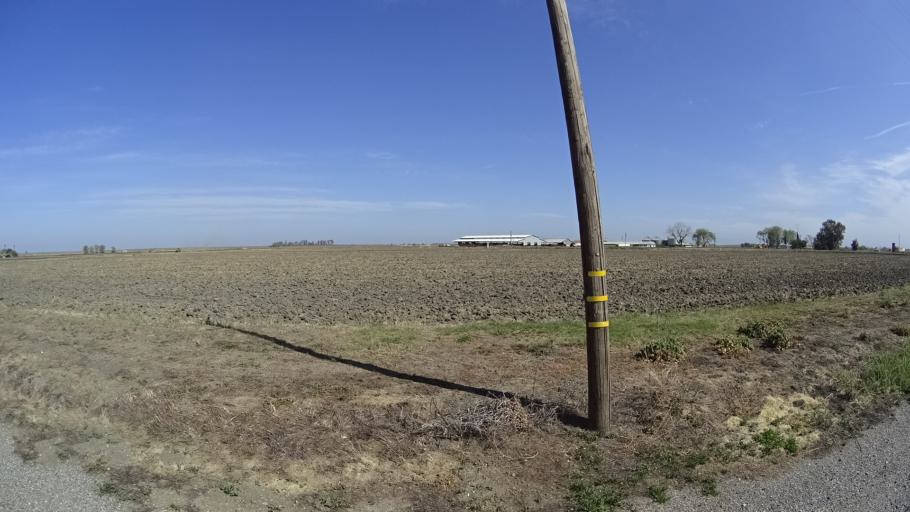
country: US
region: California
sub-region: Glenn County
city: Hamilton City
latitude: 39.6157
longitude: -122.0681
